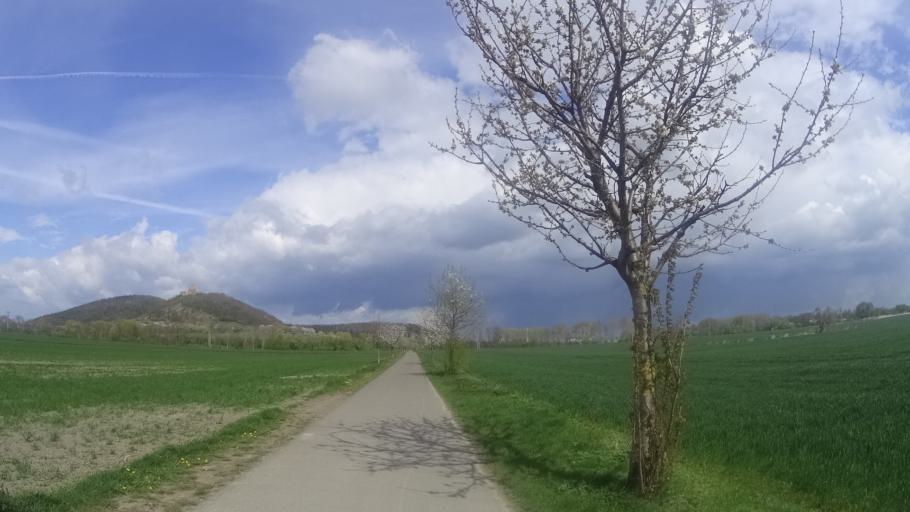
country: DE
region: Thuringia
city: Wandersleben
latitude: 50.8731
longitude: 10.8497
